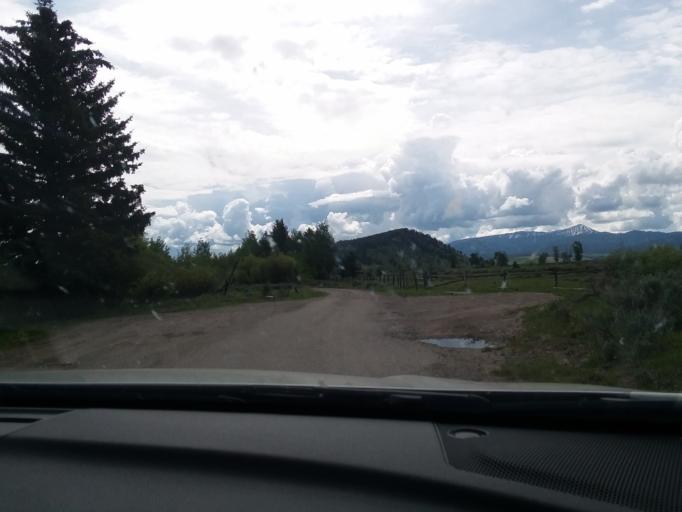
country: US
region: Wyoming
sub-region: Teton County
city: Jackson
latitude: 43.8303
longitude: -110.5132
